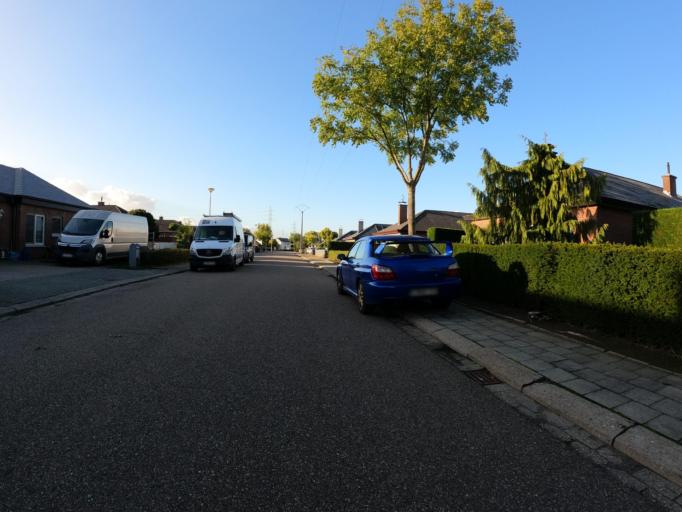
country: BE
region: Flanders
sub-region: Provincie Antwerpen
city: Heist-op-den-Berg
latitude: 51.0511
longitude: 4.7078
